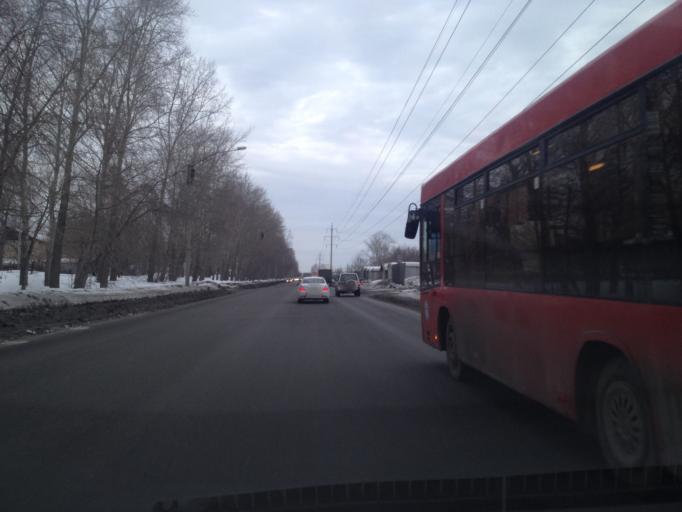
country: RU
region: Sverdlovsk
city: Sovkhoznyy
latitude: 56.7666
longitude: 60.5934
